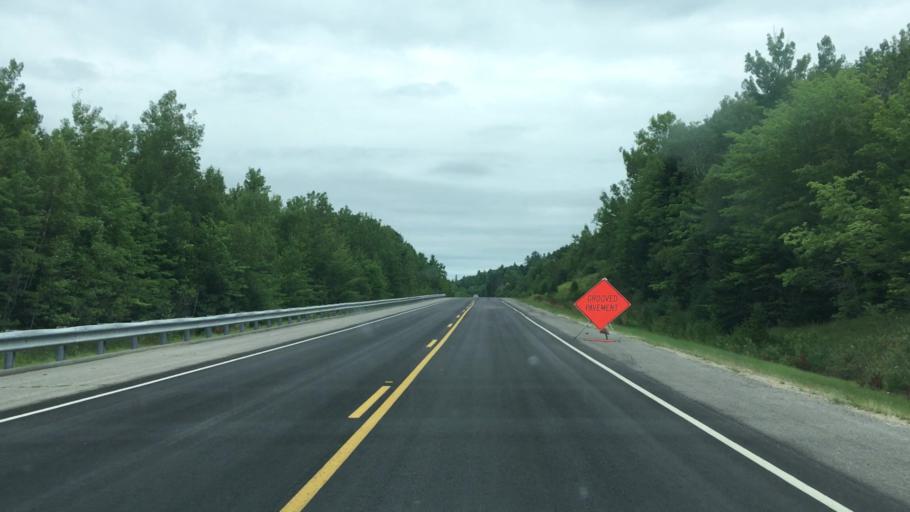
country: US
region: Maine
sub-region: Washington County
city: Cherryfield
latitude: 44.8910
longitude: -67.8563
